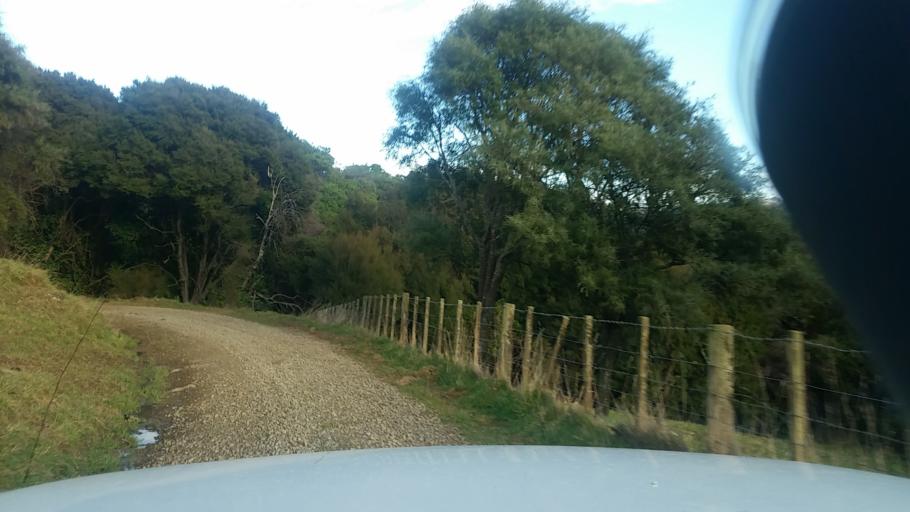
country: NZ
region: Canterbury
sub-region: Christchurch City
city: Christchurch
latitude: -43.7599
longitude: 172.9915
